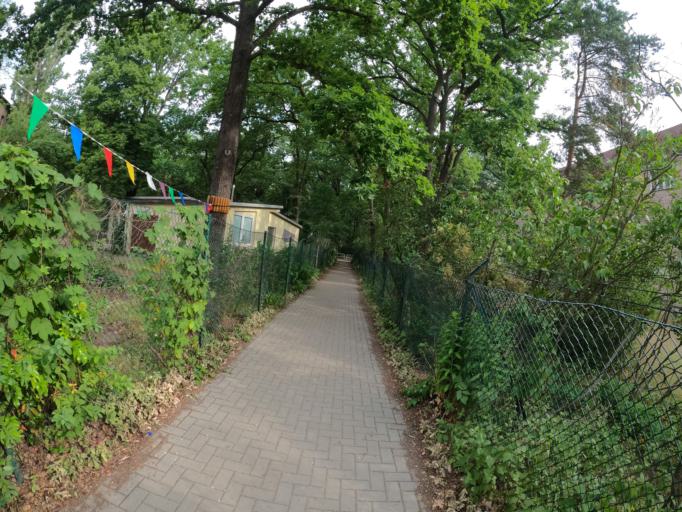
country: DE
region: Berlin
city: Siemensstadt
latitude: 52.5416
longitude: 13.2675
